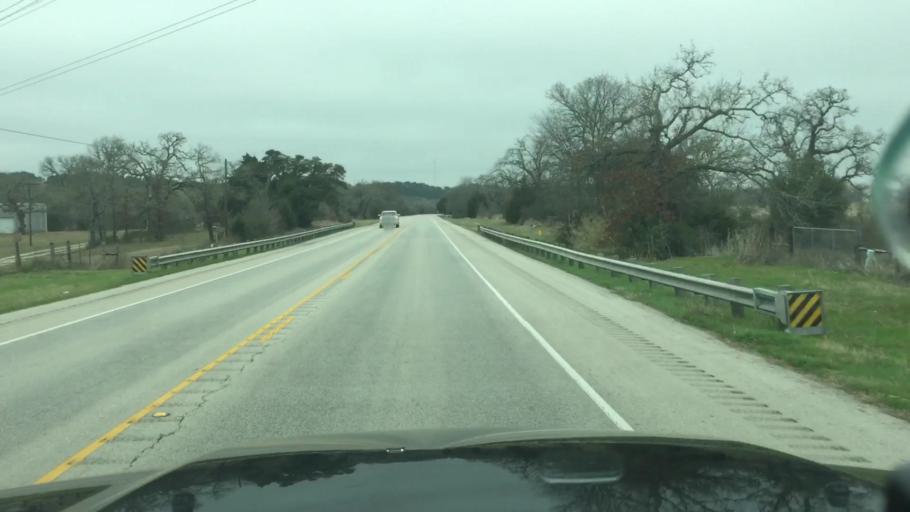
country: US
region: Texas
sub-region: Fayette County
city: La Grange
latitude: 30.0280
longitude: -96.9049
